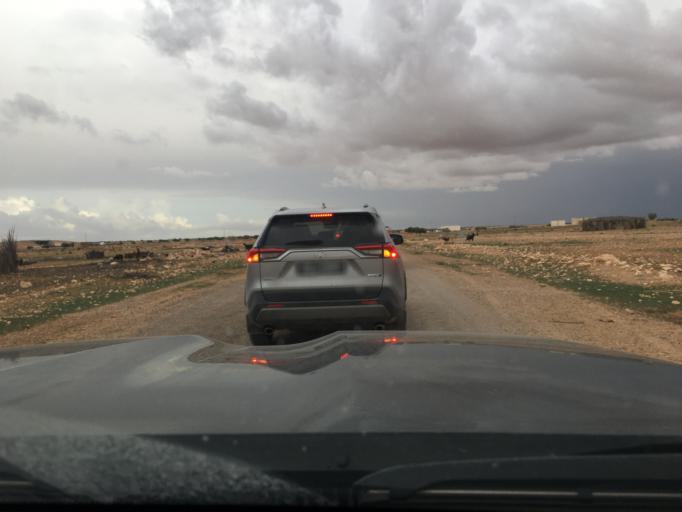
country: TN
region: Madanin
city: Medenine
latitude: 33.2929
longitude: 10.6078
